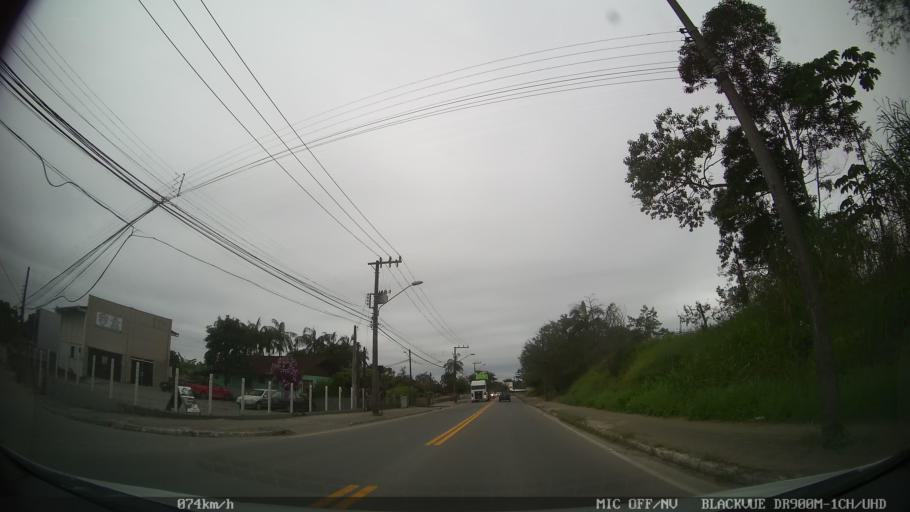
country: BR
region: Santa Catarina
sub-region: Joinville
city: Joinville
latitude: -26.2843
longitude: -48.9214
